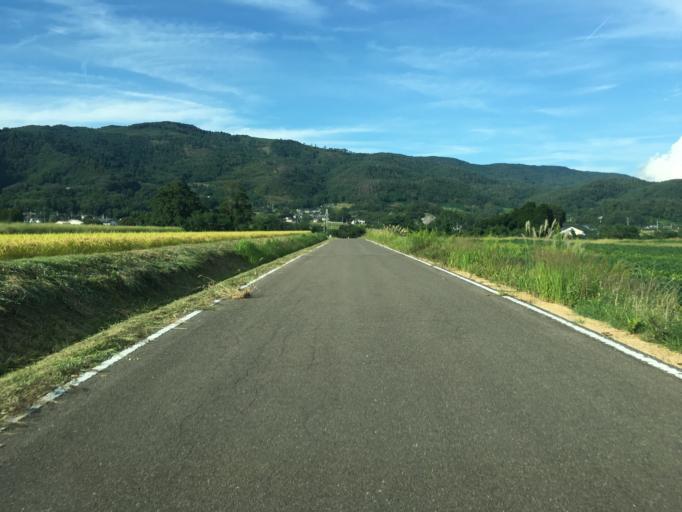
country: JP
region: Fukushima
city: Hobaramachi
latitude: 37.8841
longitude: 140.5266
